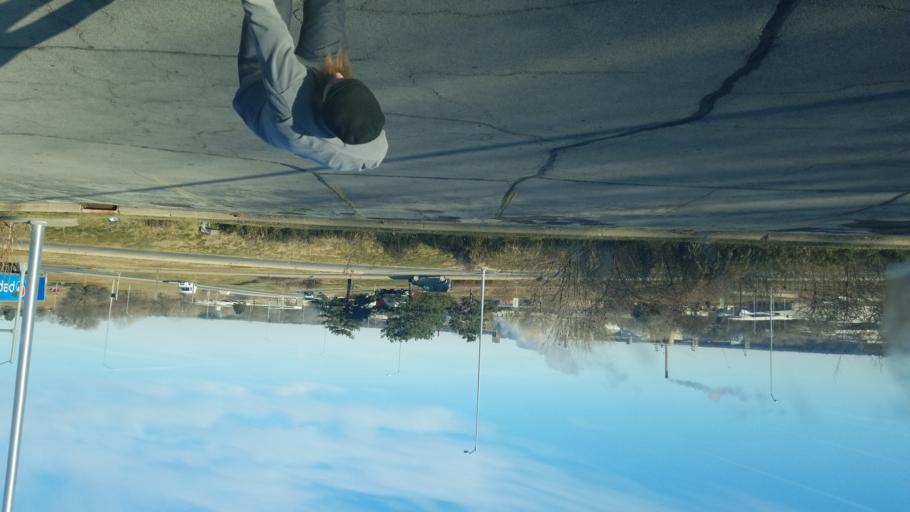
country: US
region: Iowa
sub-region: Polk County
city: Des Moines
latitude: 41.6273
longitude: -93.5721
